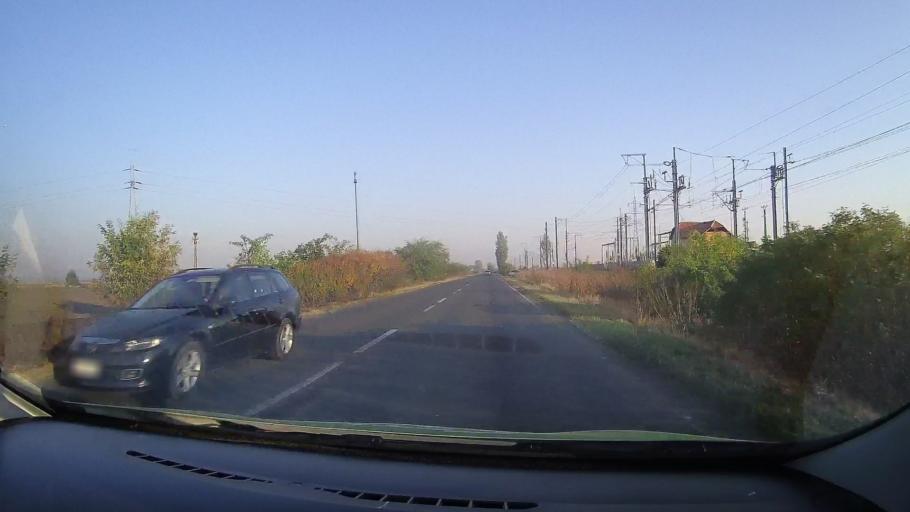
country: RO
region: Arad
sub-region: Comuna Sofronea
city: Sofronea
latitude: 46.2608
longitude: 21.3173
